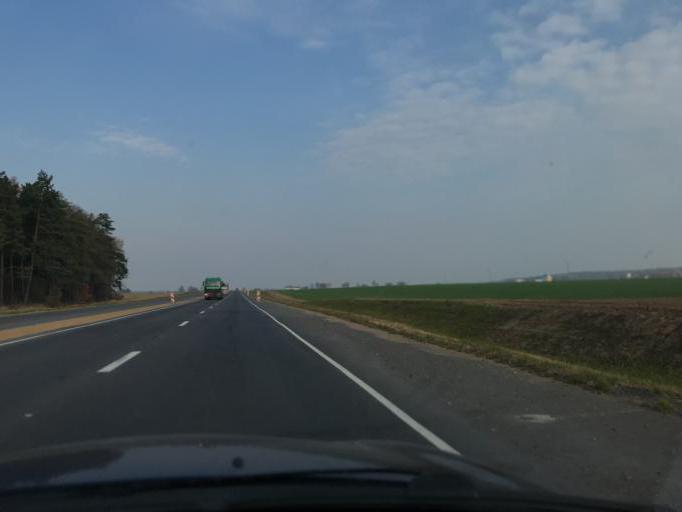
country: BY
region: Grodnenskaya
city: Shchuchin
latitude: 53.7201
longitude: 24.9619
